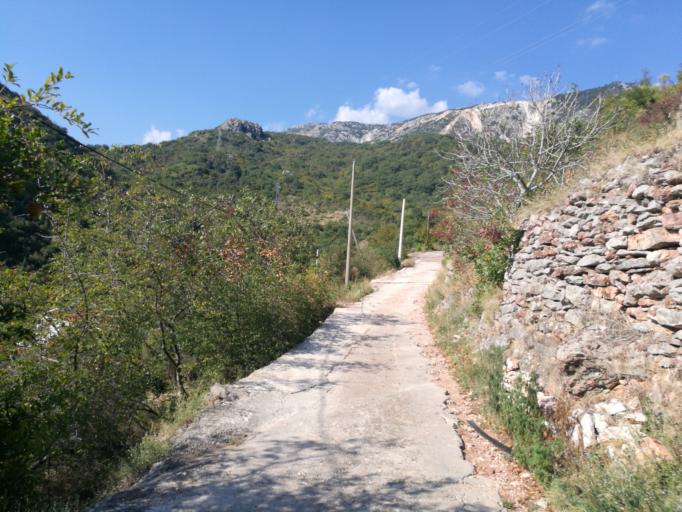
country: ME
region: Budva
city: Budva
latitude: 42.2853
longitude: 18.8859
